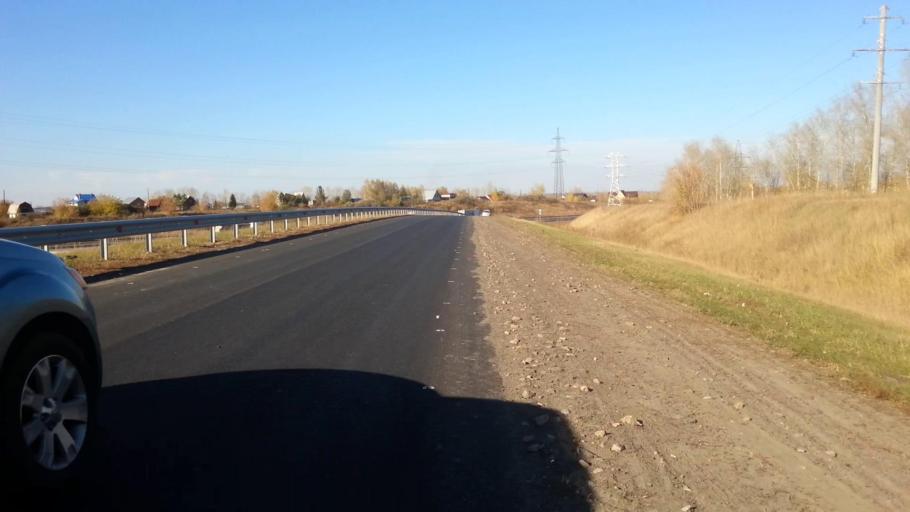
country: RU
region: Altai Krai
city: Sannikovo
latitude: 53.3403
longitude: 83.9388
